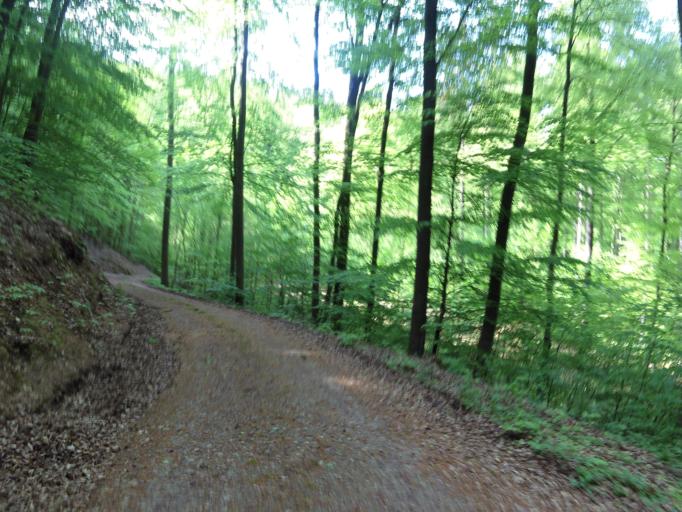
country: DE
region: Thuringia
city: Wolfsburg-Unkeroda
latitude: 50.9563
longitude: 10.2832
